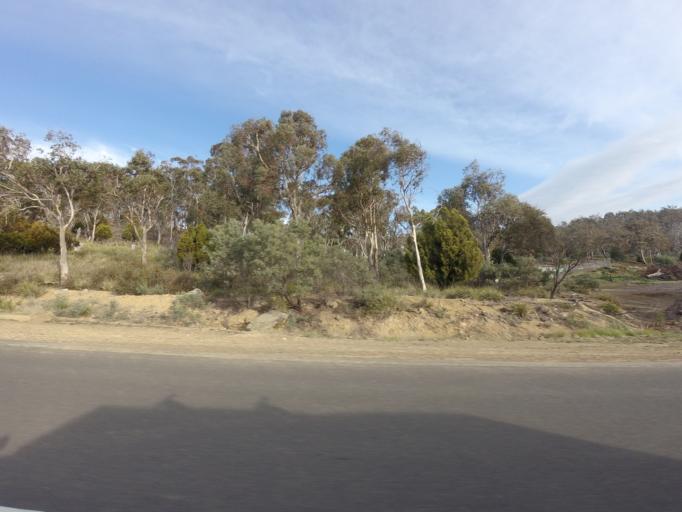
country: AU
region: Tasmania
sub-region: Derwent Valley
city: New Norfolk
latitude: -42.3859
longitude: 147.0387
